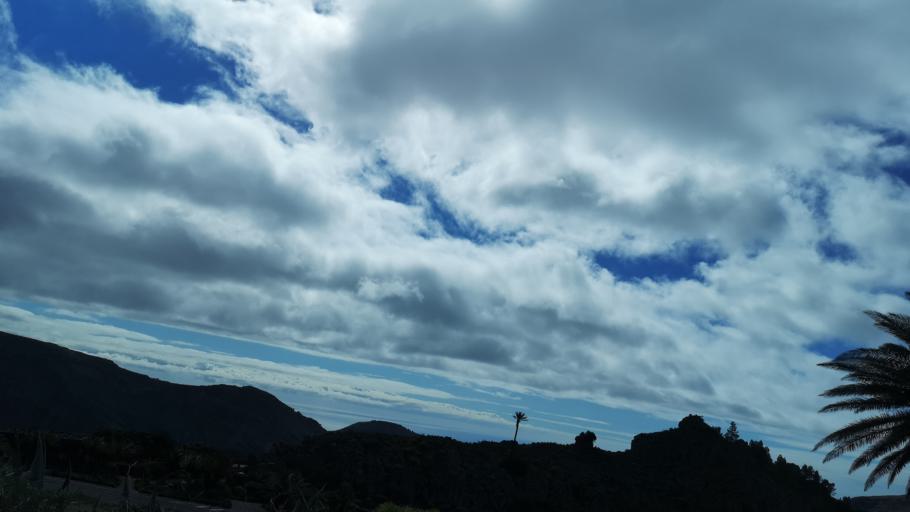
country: ES
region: Canary Islands
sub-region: Provincia de Santa Cruz de Tenerife
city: Vallehermosa
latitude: 28.1207
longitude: -17.3155
